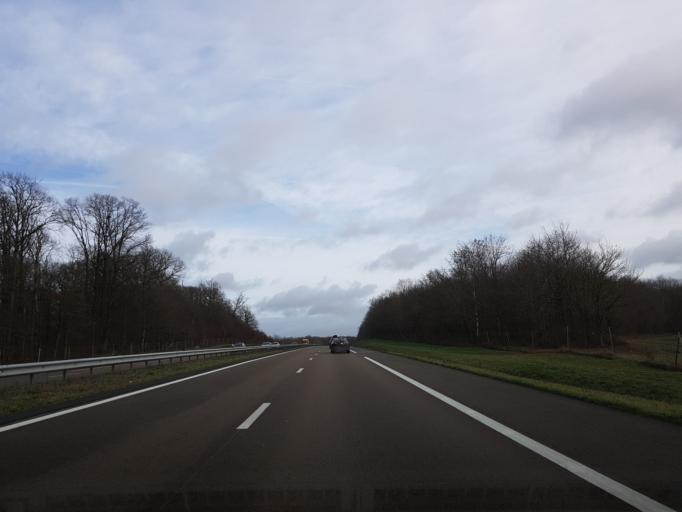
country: FR
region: Champagne-Ardenne
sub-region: Departement de l'Aube
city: Bar-sur-Seine
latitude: 48.1781
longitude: 4.3779
